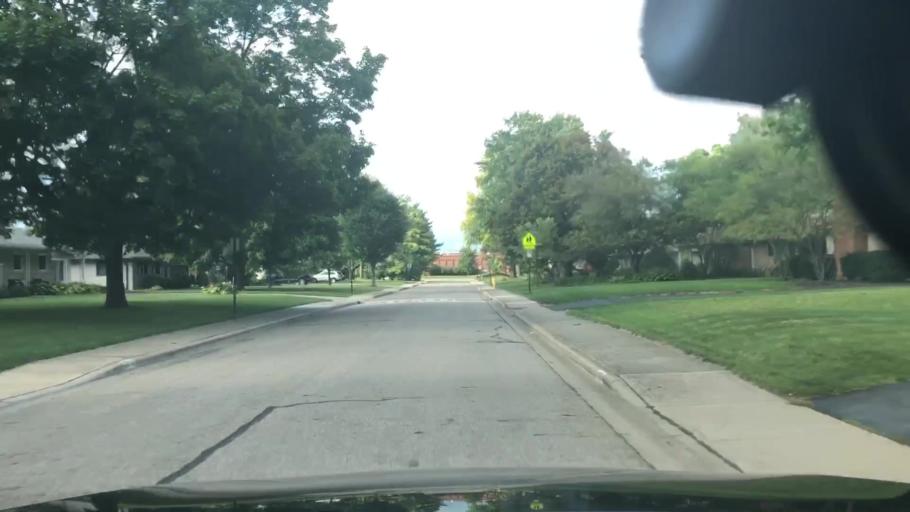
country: US
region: Ohio
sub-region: Franklin County
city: Upper Arlington
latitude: 40.0125
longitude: -83.0542
